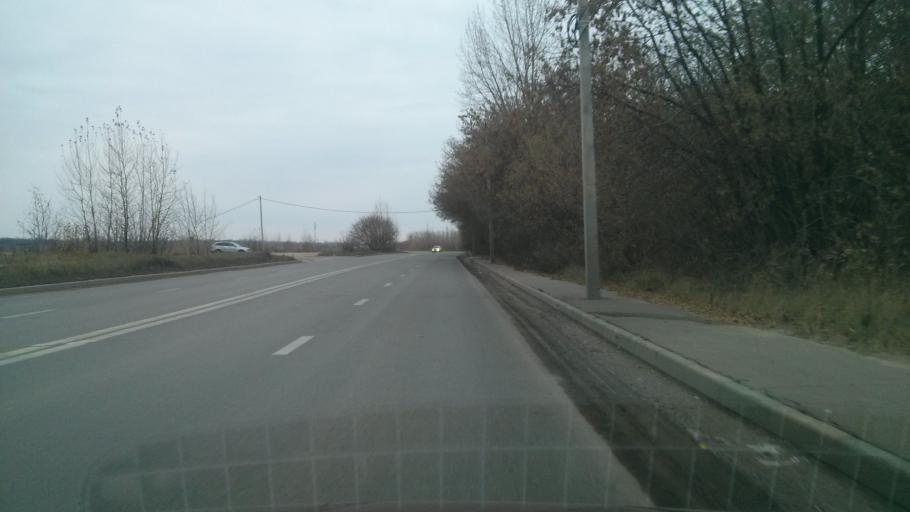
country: RU
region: Nizjnij Novgorod
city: Bor
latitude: 56.3148
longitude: 44.0844
